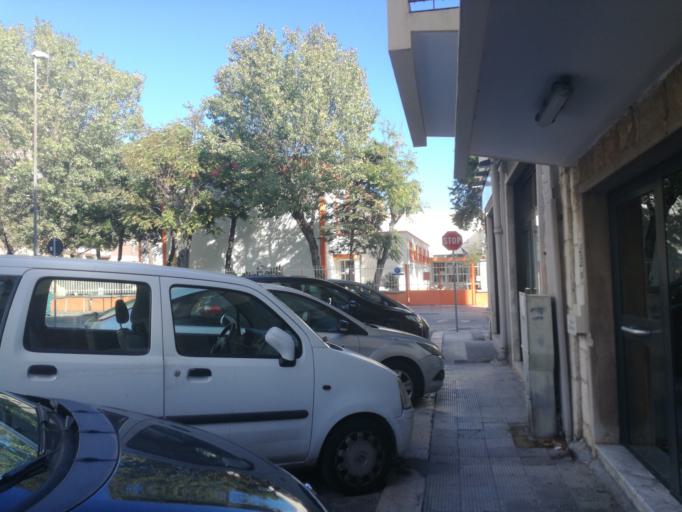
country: IT
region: Apulia
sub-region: Provincia di Bari
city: Bari
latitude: 41.1141
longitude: 16.8951
